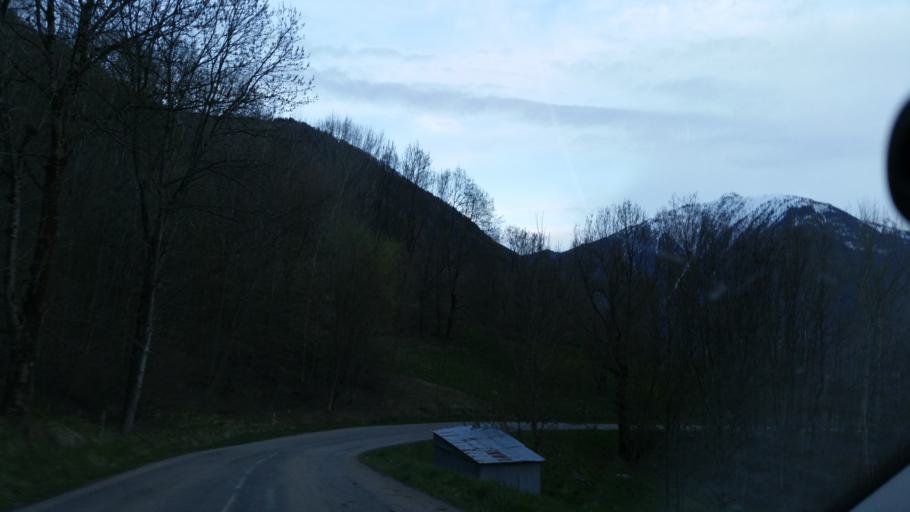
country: FR
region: Rhone-Alpes
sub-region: Departement de la Savoie
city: La Chambre
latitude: 45.3725
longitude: 6.3218
